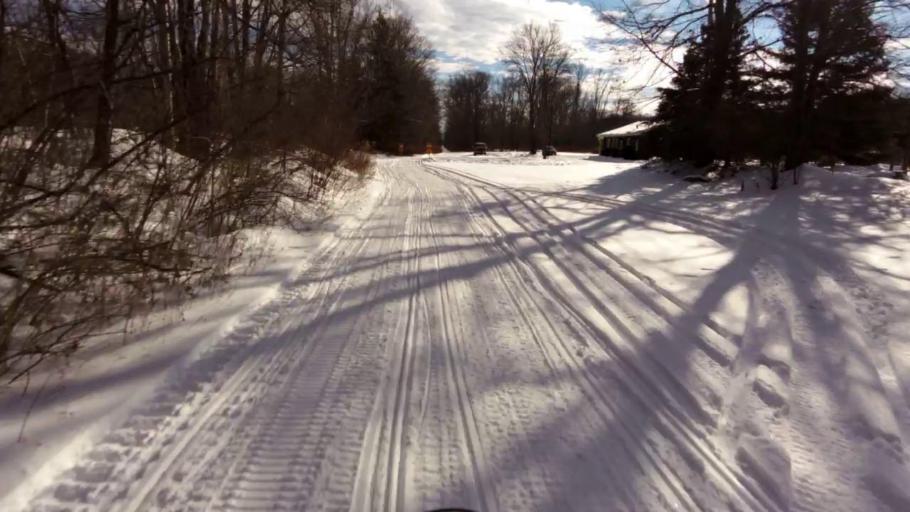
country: US
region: Pennsylvania
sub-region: McKean County
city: Foster Brook
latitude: 42.0505
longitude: -78.6361
